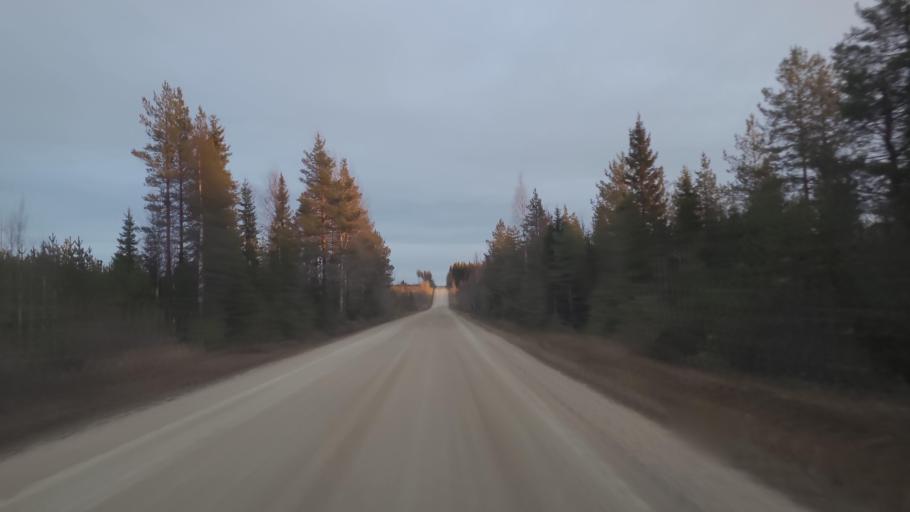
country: FI
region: Lapland
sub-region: Kemi-Tornio
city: Tervola
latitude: 66.0624
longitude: 24.9241
